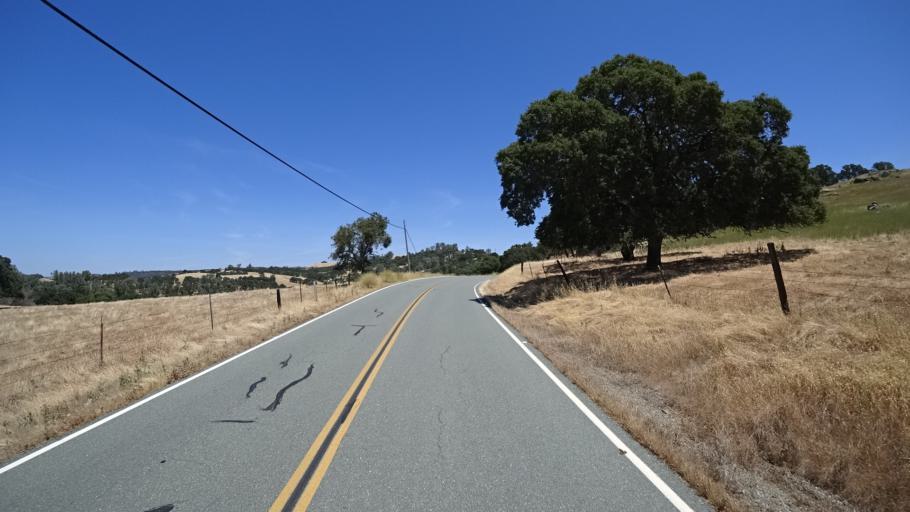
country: US
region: California
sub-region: Calaveras County
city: Valley Springs
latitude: 38.2378
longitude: -120.7928
